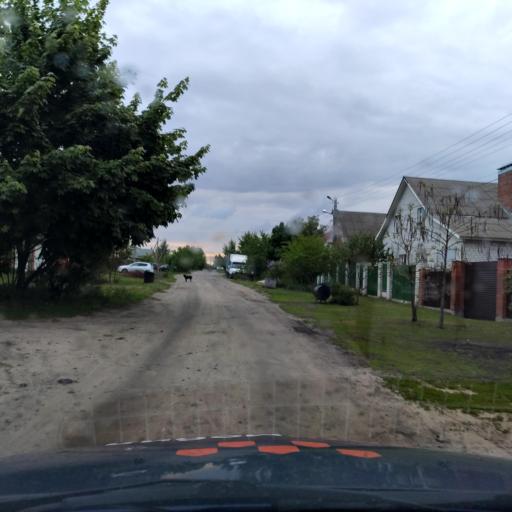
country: RU
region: Voronezj
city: Maslovka
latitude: 51.5455
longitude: 39.2396
